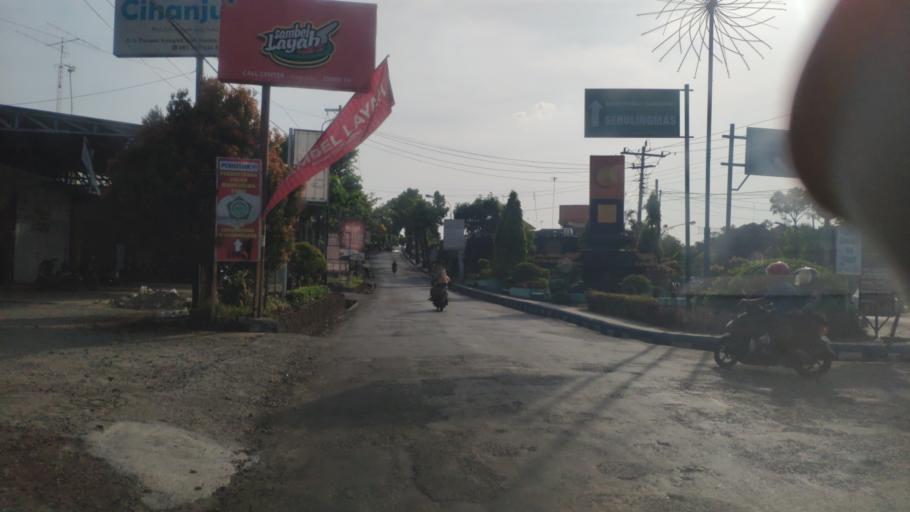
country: ID
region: Central Java
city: Wonosobo
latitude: -7.3955
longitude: 109.7040
